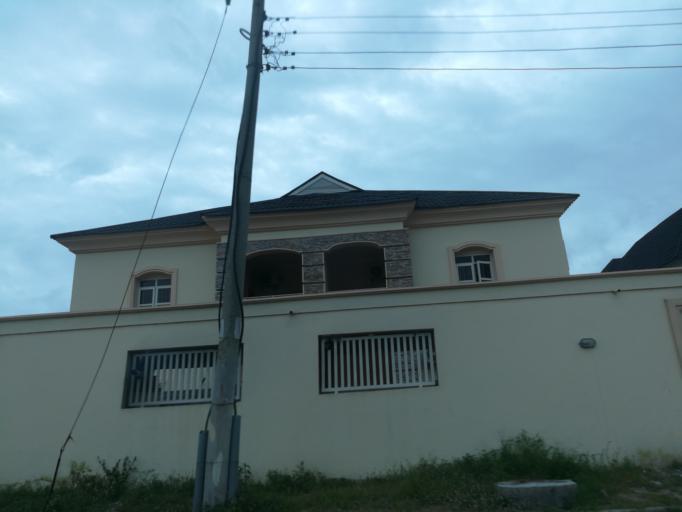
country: NG
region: Lagos
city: Ikoyi
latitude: 6.4387
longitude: 3.4685
